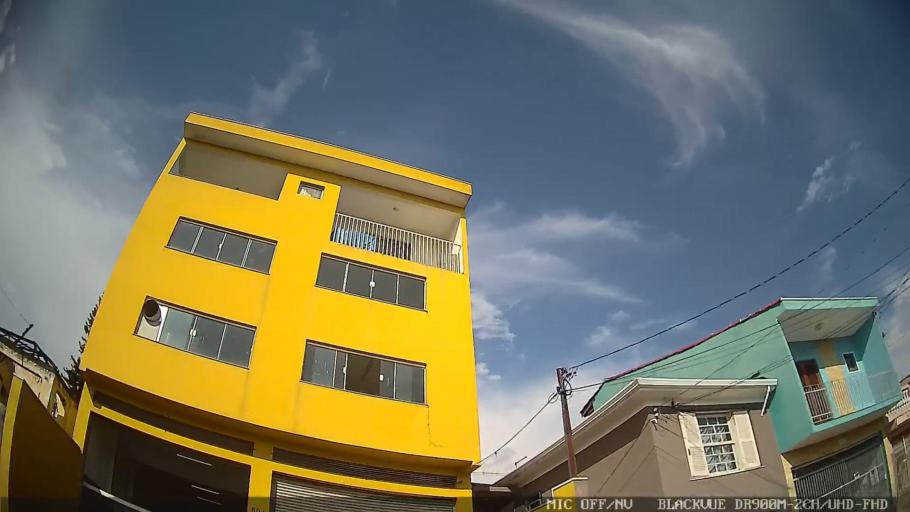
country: BR
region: Sao Paulo
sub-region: Braganca Paulista
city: Braganca Paulista
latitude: -22.9557
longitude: -46.5293
